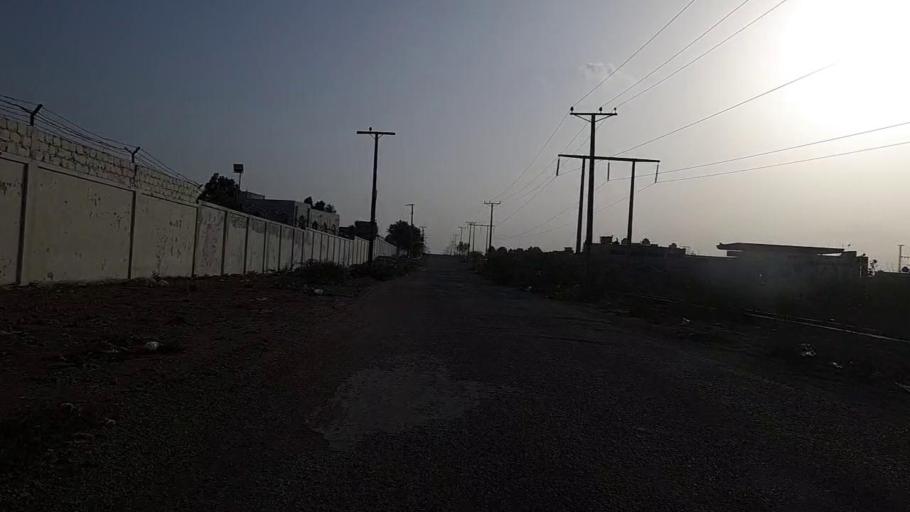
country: PK
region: Sindh
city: Thatta
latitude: 25.1786
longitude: 67.8104
